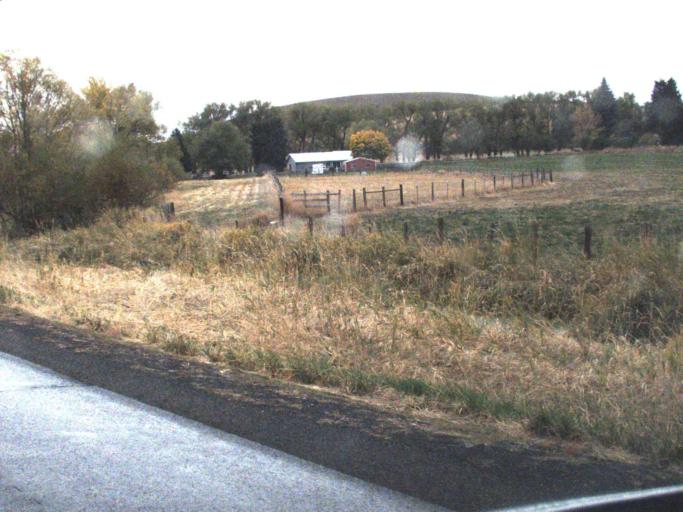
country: US
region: Washington
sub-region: Whitman County
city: Colfax
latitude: 46.8330
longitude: -117.3309
